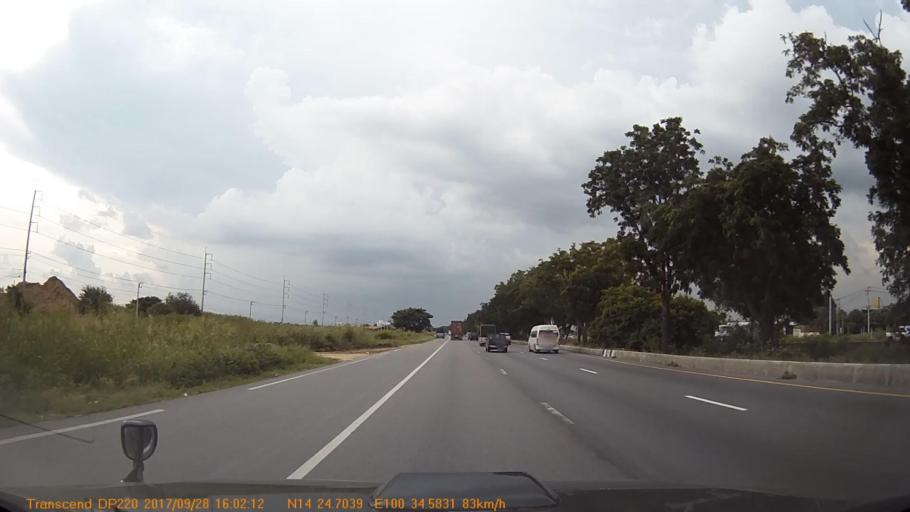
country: TH
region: Phra Nakhon Si Ayutthaya
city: Bang Pahan
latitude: 14.4116
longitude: 100.5765
